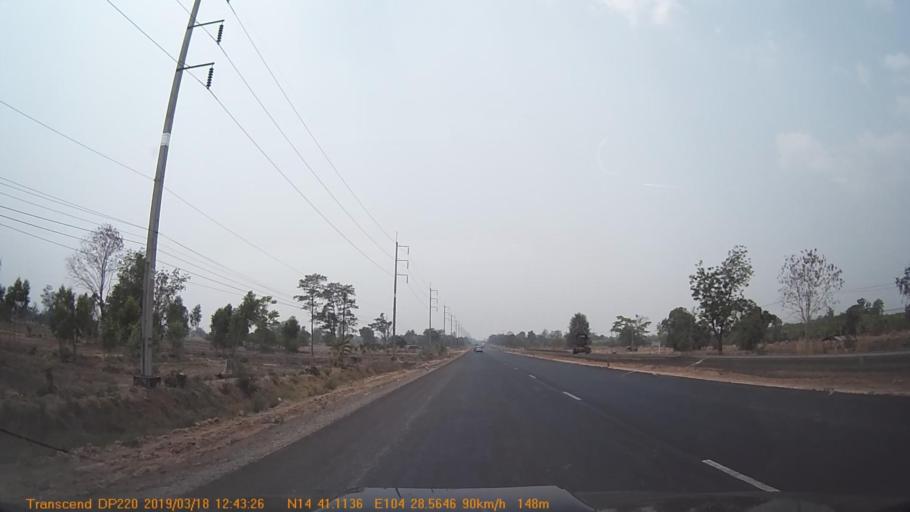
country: TH
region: Sisaket
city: Khun Han
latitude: 14.6853
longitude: 104.4756
